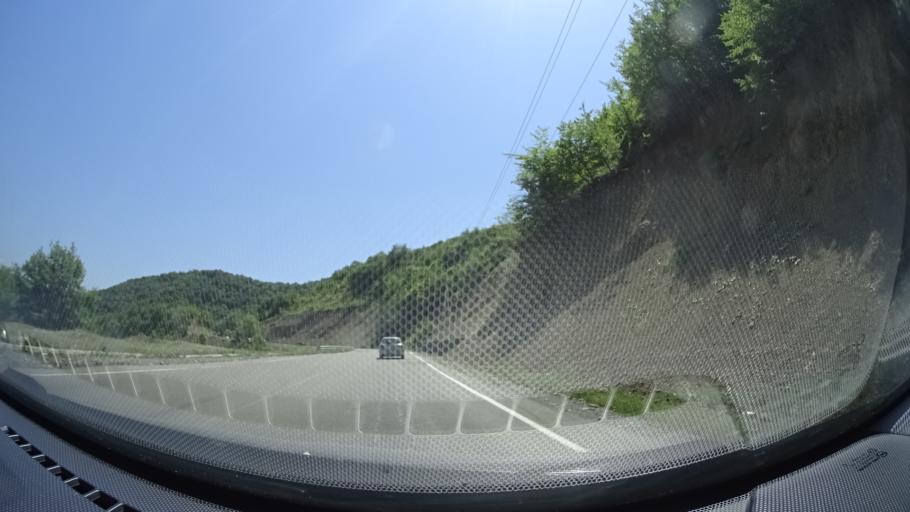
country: GE
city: Zhinvali
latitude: 42.1563
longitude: 44.7184
